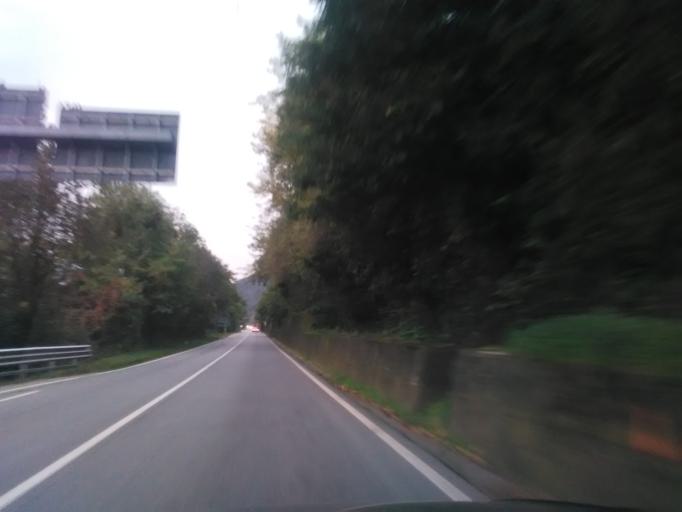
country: IT
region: Piedmont
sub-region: Provincia di Vercelli
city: Borgosesia
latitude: 45.7110
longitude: 8.2692
